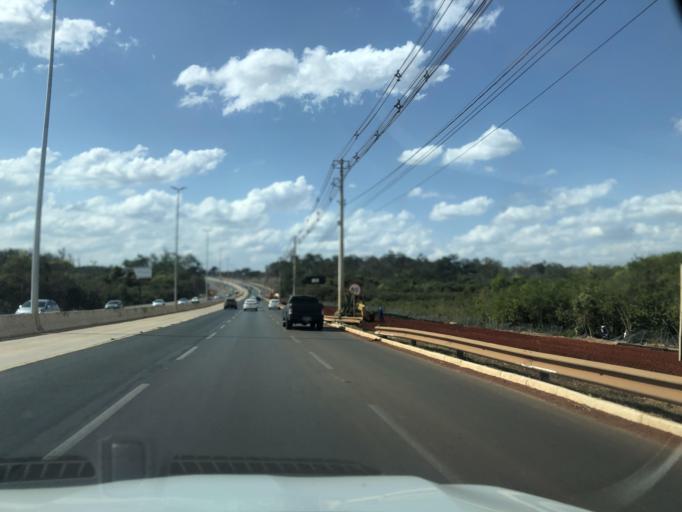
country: BR
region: Federal District
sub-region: Brasilia
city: Brasilia
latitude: -15.8546
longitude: -47.9321
